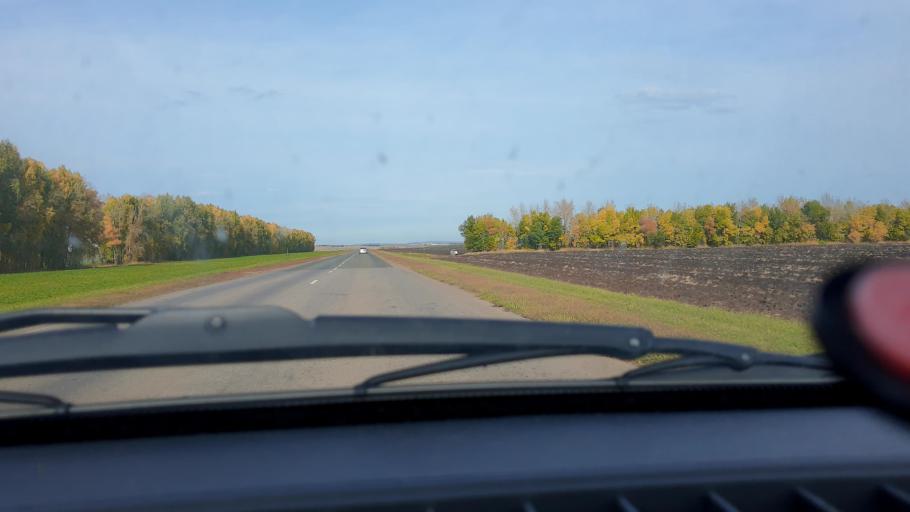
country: RU
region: Bashkortostan
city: Chekmagush
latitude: 54.9700
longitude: 54.5692
